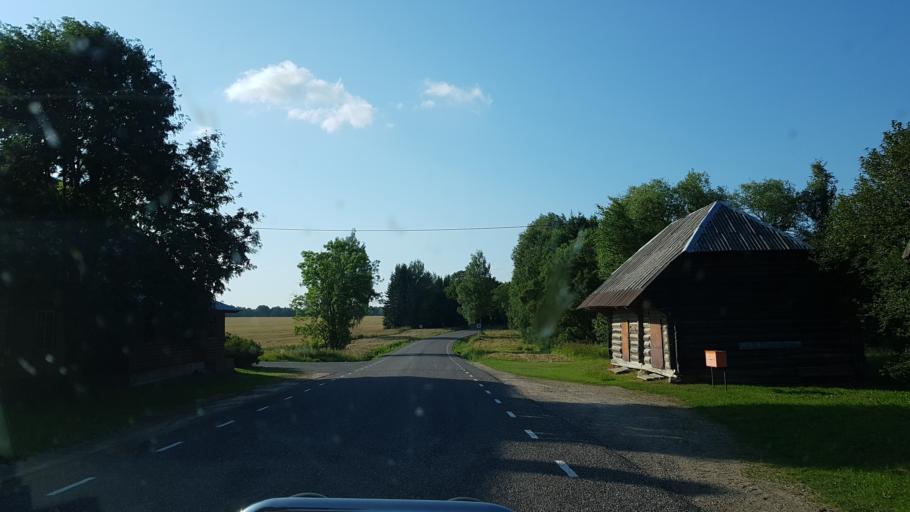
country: EE
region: Polvamaa
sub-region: Polva linn
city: Polva
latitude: 58.0018
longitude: 26.9281
